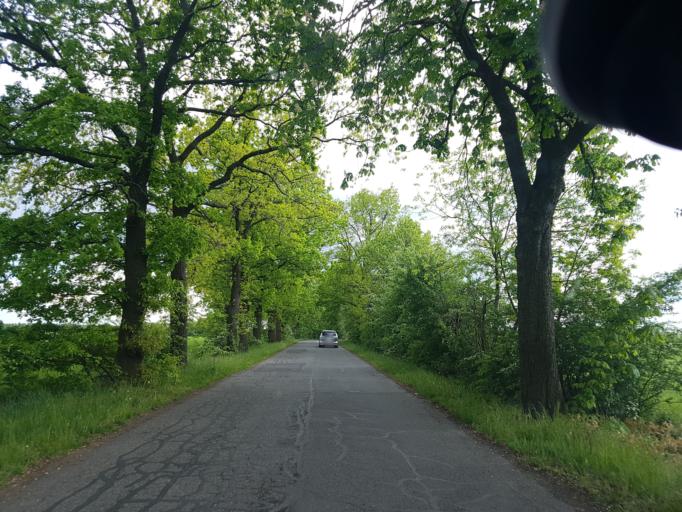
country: DE
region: Brandenburg
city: Grossraschen
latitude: 51.5854
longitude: 14.0622
